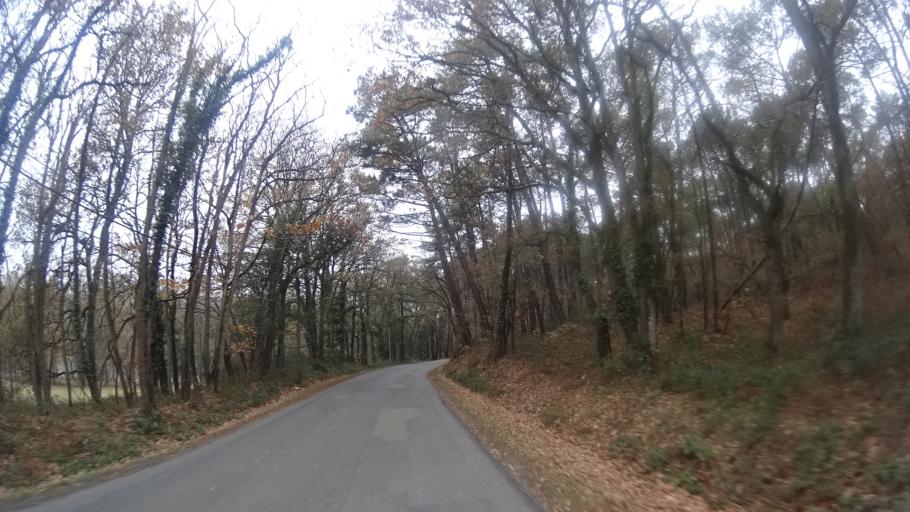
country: FR
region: Brittany
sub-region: Departement d'Ille-et-Vilaine
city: Bains-sur-Oust
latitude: 47.6800
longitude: -2.0805
